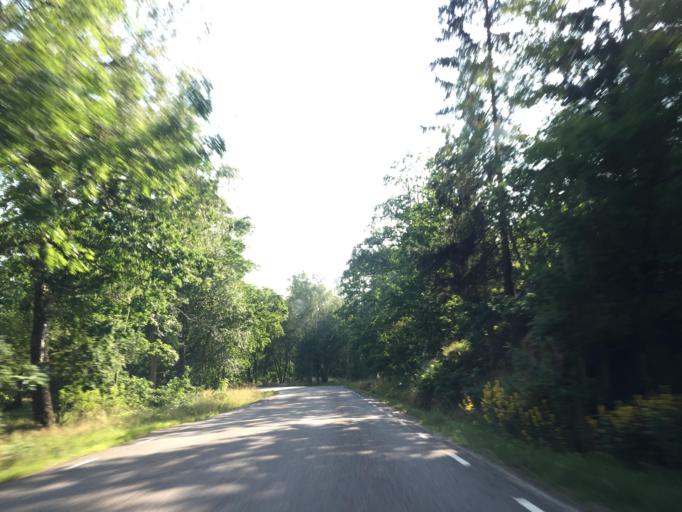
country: SE
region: Vaestra Goetaland
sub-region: Trollhattan
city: Trollhattan
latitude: 58.2620
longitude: 12.2296
